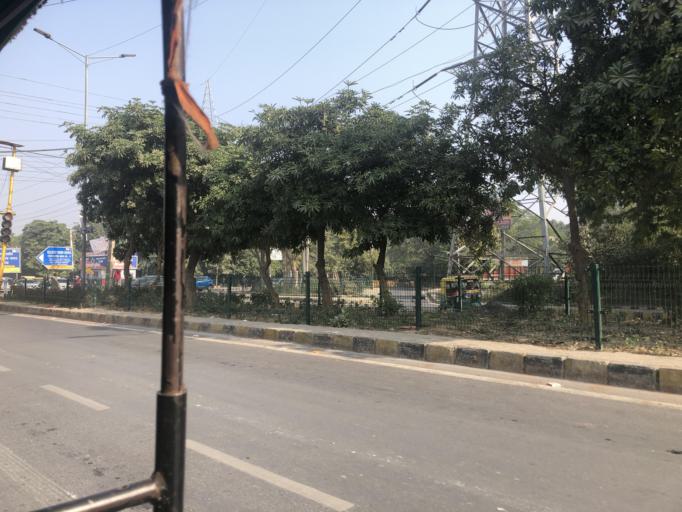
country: IN
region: Haryana
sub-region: Gurgaon
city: Gurgaon
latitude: 28.4295
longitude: 77.0912
